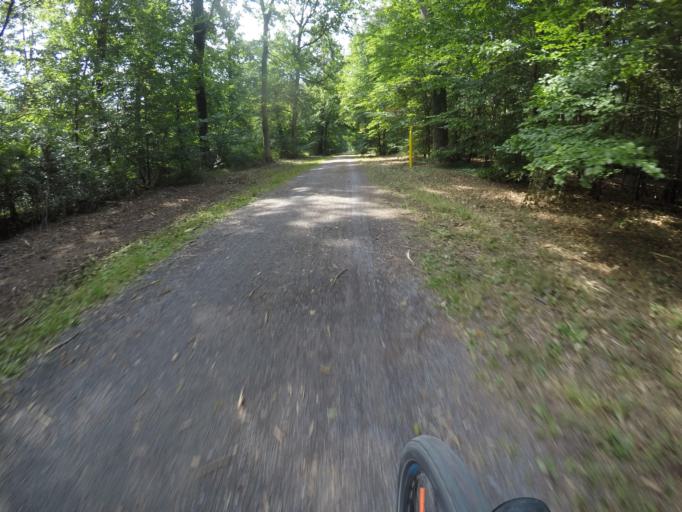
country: DE
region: Baden-Wuerttemberg
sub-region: Karlsruhe Region
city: Reilingen
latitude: 49.2796
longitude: 8.5697
